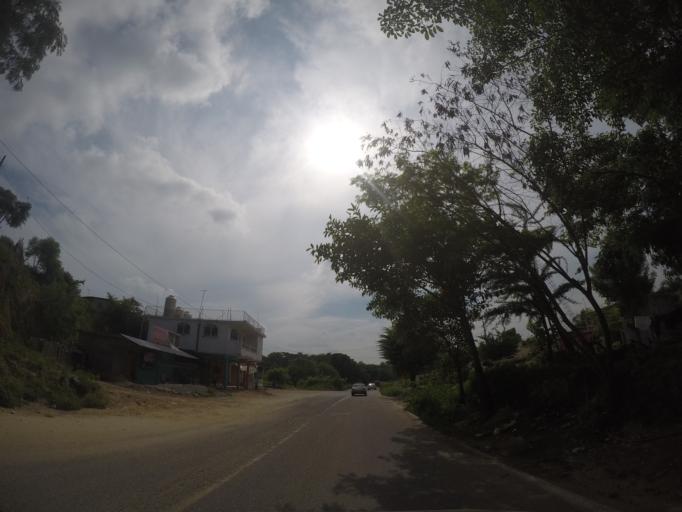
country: MX
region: Guerrero
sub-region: Acapulco de Juarez
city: Cerro de Piedra
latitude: 16.7749
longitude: -99.6266
